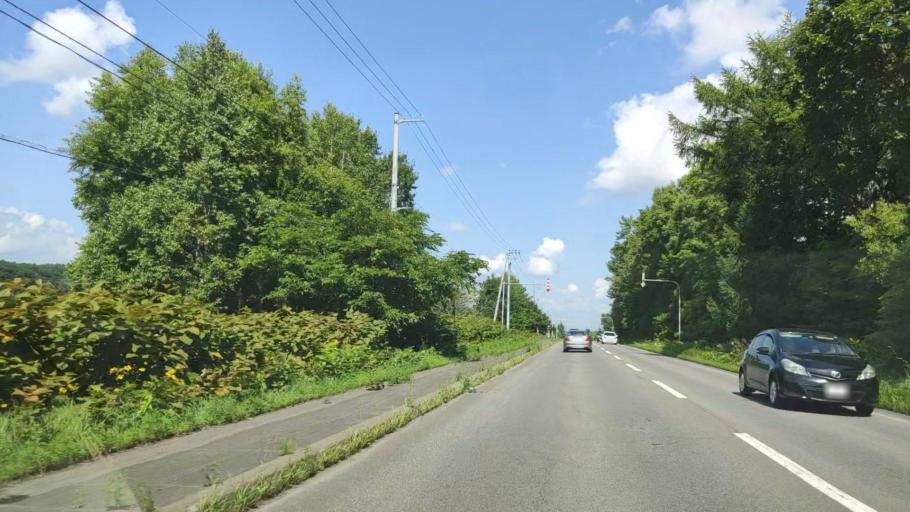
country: JP
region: Hokkaido
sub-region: Asahikawa-shi
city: Asahikawa
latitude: 43.6339
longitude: 142.4573
